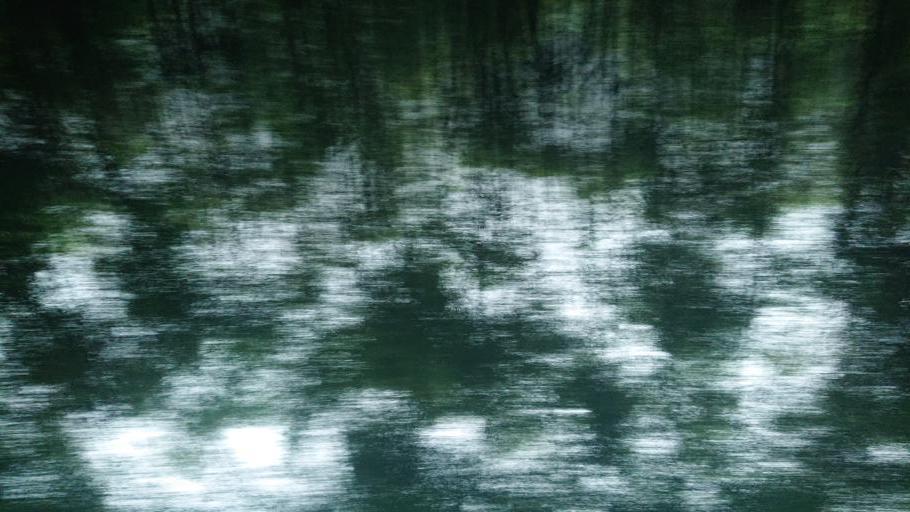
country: TW
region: Taiwan
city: Lugu
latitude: 23.5115
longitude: 120.7014
